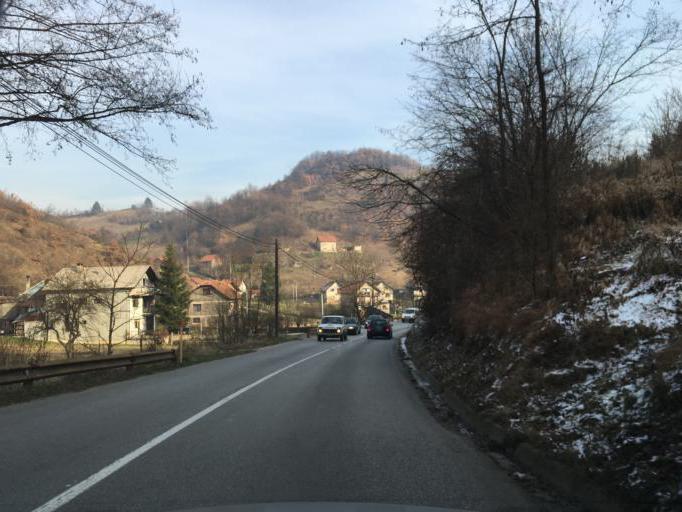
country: BA
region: Federation of Bosnia and Herzegovina
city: Lokvine
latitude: 44.1899
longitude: 17.8554
